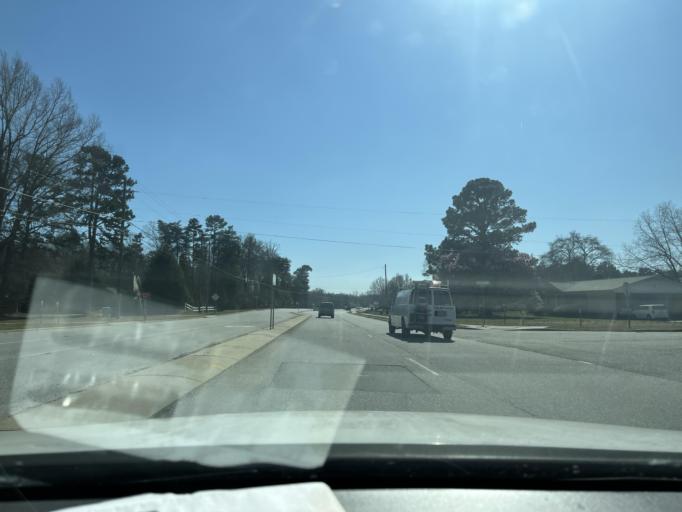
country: US
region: North Carolina
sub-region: Guilford County
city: Jamestown
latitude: 36.0290
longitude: -79.9229
